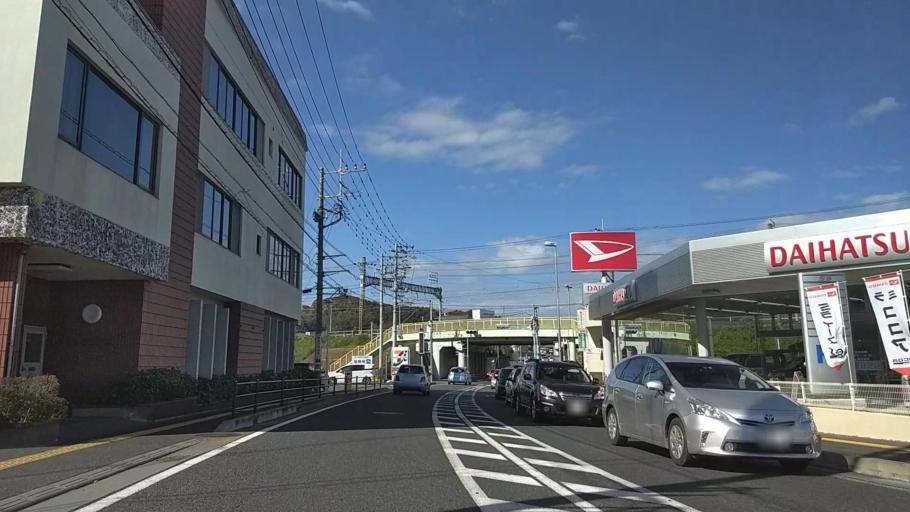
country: JP
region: Kanagawa
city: Ninomiya
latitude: 35.2995
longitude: 139.2610
